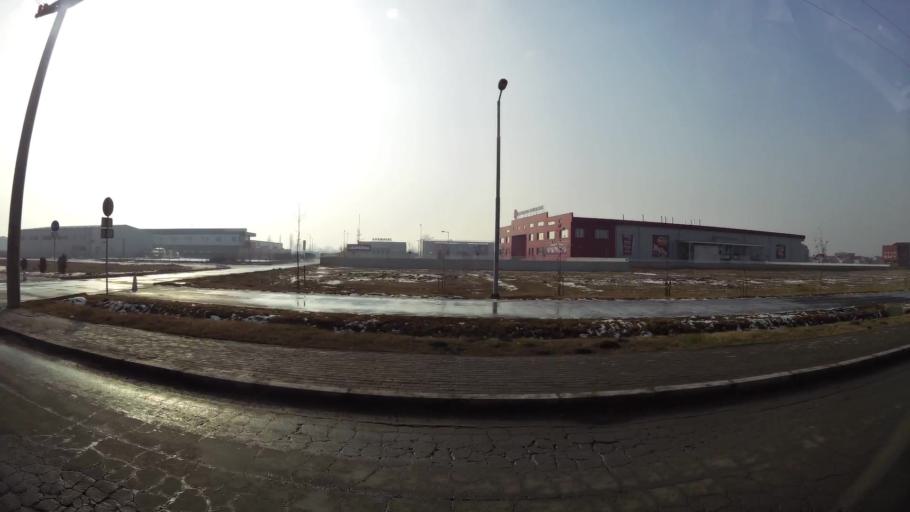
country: MK
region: Ilinden
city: Marino
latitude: 41.9850
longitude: 21.5900
